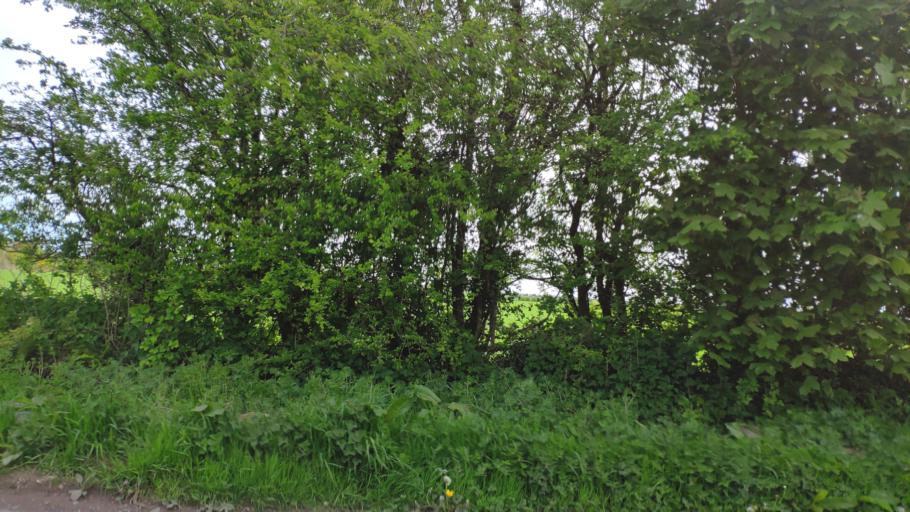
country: IE
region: Munster
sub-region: County Cork
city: Blarney
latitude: 51.9778
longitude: -8.5134
